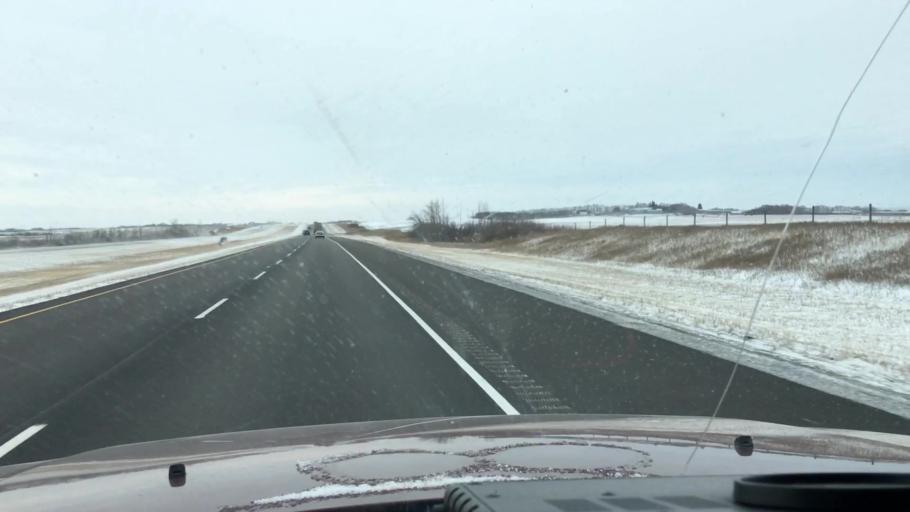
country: CA
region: Saskatchewan
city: Saskatoon
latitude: 51.6950
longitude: -106.4594
